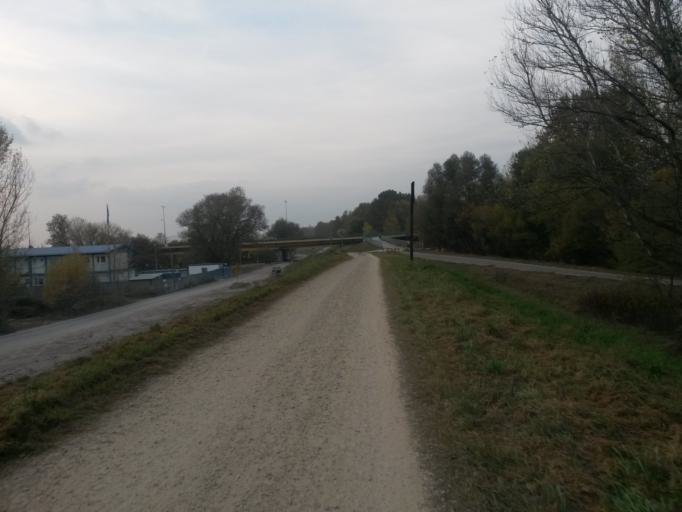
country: PL
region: Masovian Voivodeship
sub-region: Warszawa
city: Praga Poludnie
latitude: 52.2103
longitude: 21.0901
